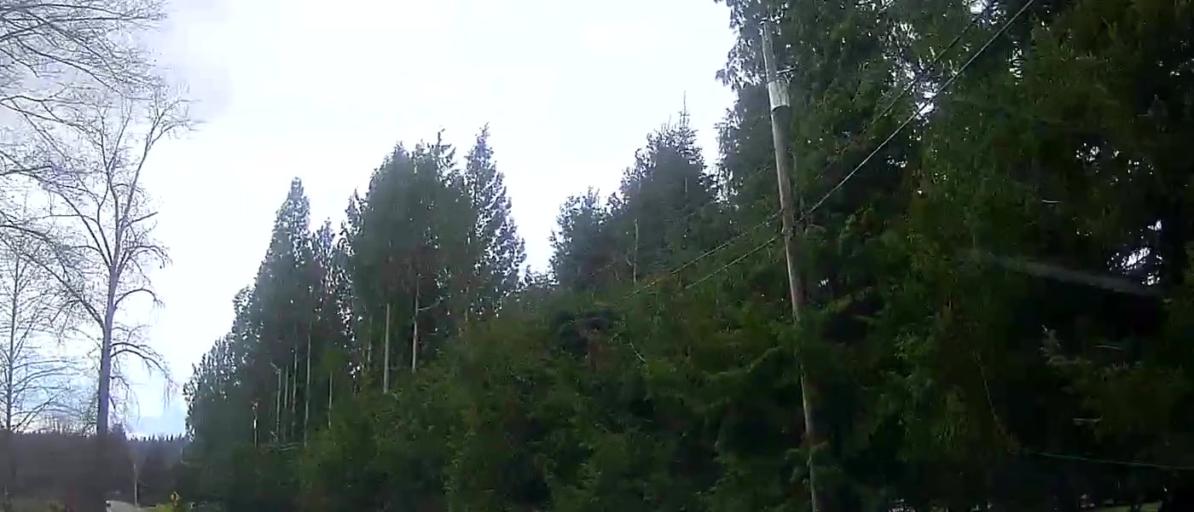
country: US
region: Washington
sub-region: Skagit County
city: Sedro-Woolley
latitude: 48.5804
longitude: -122.2929
